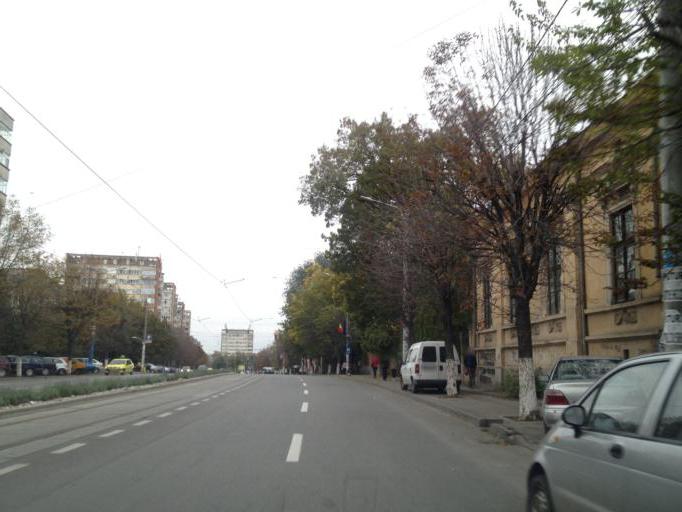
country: RO
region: Dolj
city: Craiova
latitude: 44.3247
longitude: 23.7904
